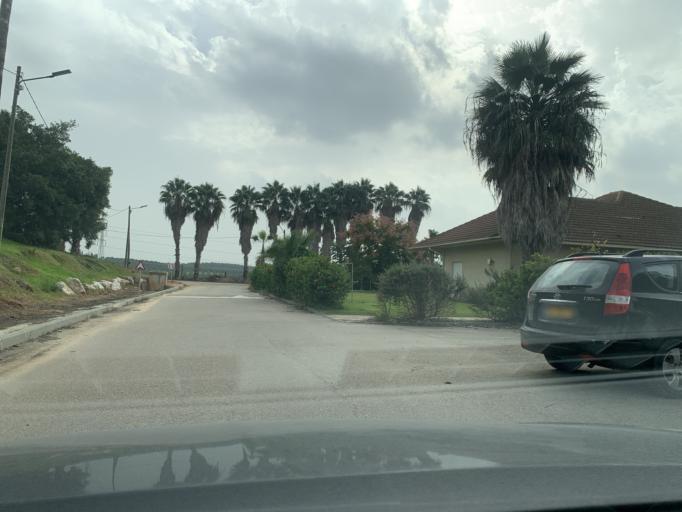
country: IL
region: Central District
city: Tirah
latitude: 32.2149
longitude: 34.9370
